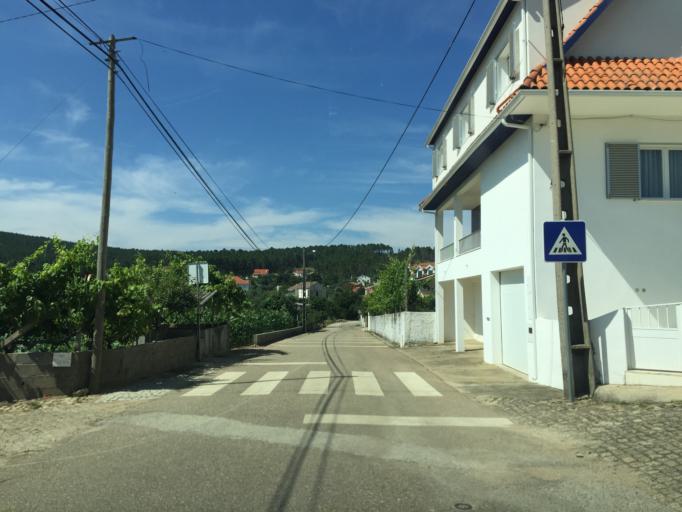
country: PT
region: Castelo Branco
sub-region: Oleiros
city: Oleiros
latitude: 39.9690
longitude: -7.8417
